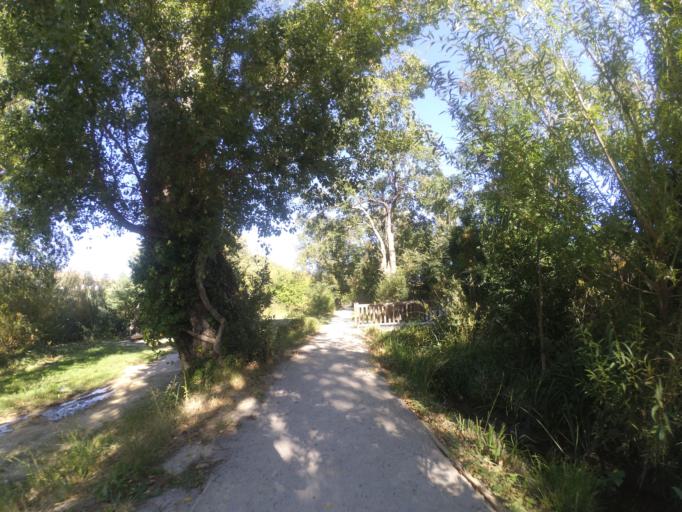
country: FR
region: Languedoc-Roussillon
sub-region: Departement des Pyrenees-Orientales
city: Perpignan
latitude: 42.6918
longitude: 2.8752
